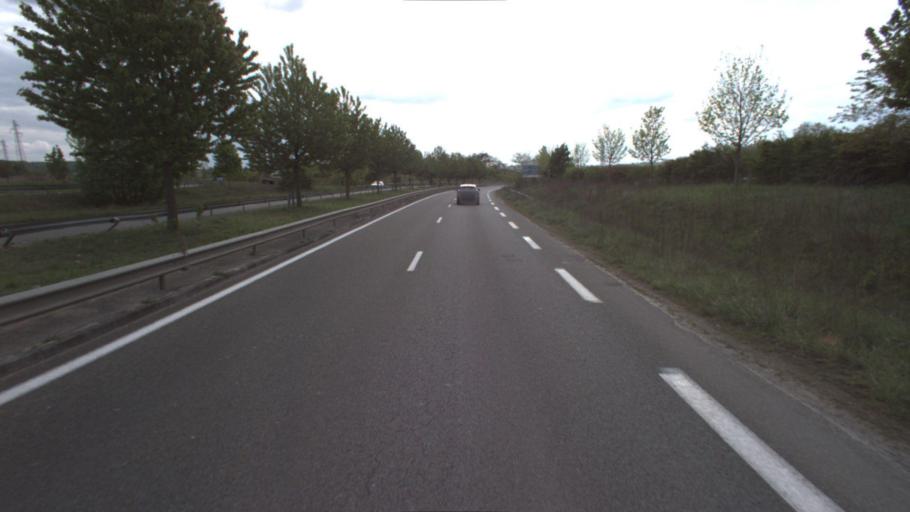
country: FR
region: Ile-de-France
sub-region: Departement de Seine-et-Marne
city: Villenoy
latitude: 48.9468
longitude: 2.8547
